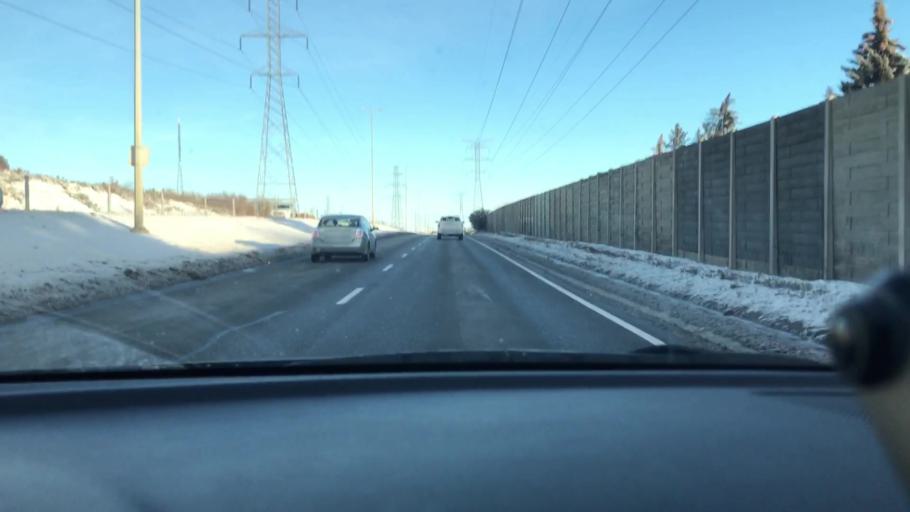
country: CA
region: Alberta
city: Calgary
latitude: 51.0465
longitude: -114.1642
